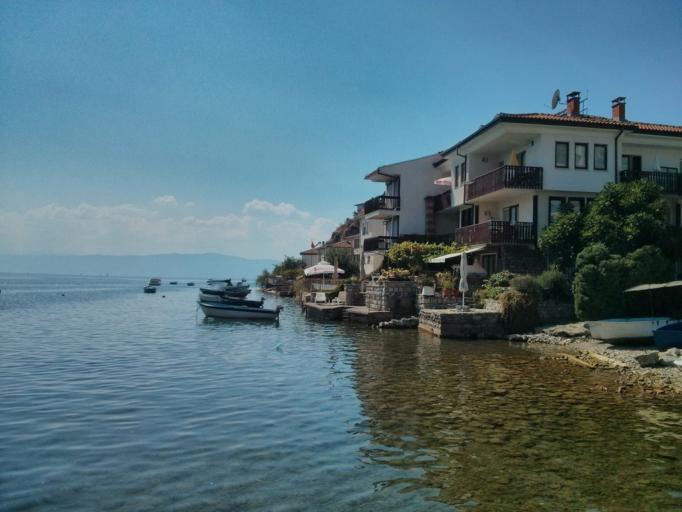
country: MK
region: Ohrid
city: Ohrid
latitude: 41.1119
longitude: 20.7957
